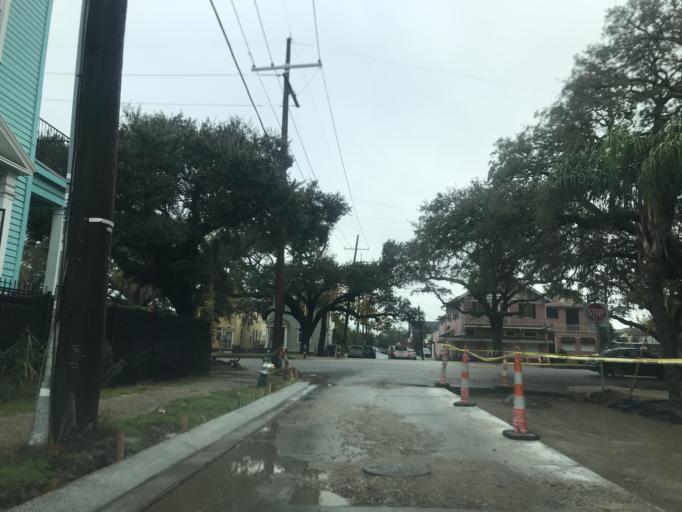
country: US
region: Louisiana
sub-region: Orleans Parish
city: New Orleans
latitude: 29.9729
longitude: -90.0973
